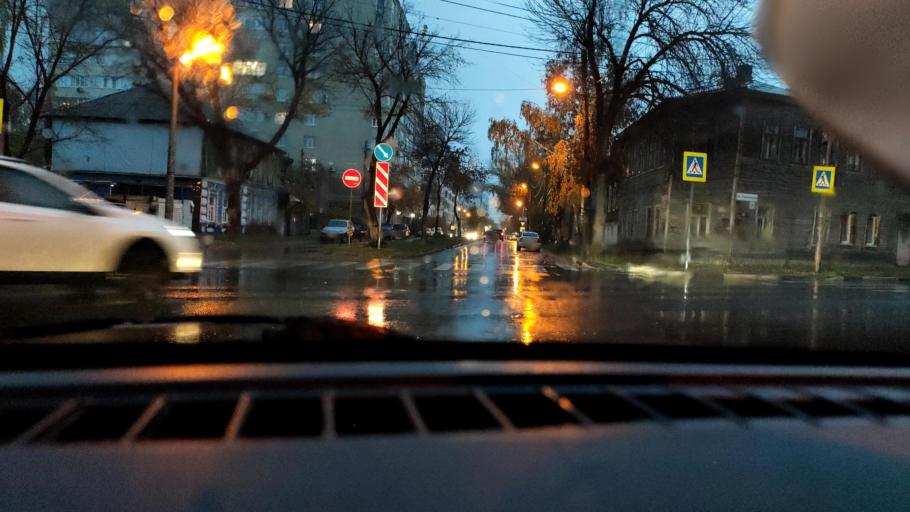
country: RU
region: Samara
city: Samara
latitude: 53.1976
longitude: 50.1138
